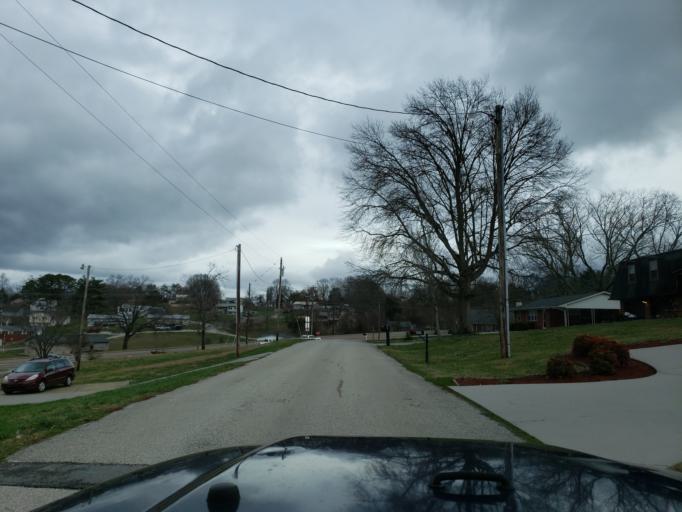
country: US
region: Tennessee
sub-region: Jefferson County
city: Jefferson City
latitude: 36.1060
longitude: -83.4859
